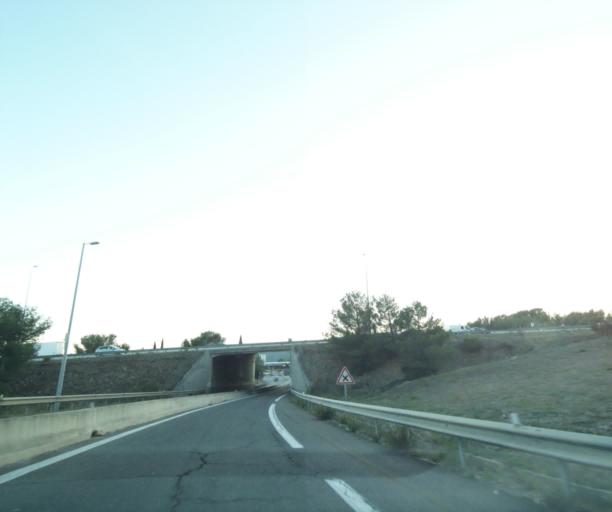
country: FR
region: Provence-Alpes-Cote d'Azur
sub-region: Departement des Bouches-du-Rhone
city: La Ciotat
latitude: 43.2042
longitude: 5.5954
